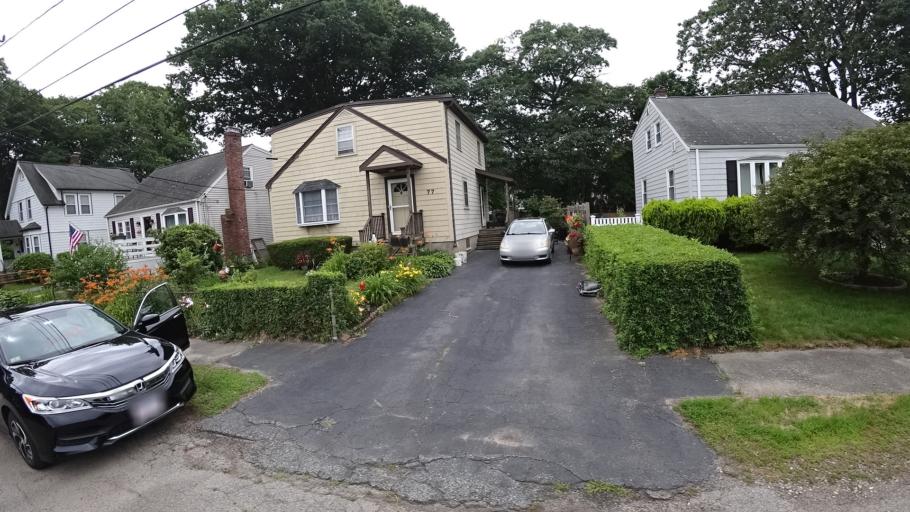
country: US
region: Massachusetts
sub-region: Norfolk County
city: Dedham
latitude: 42.2316
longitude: -71.1532
